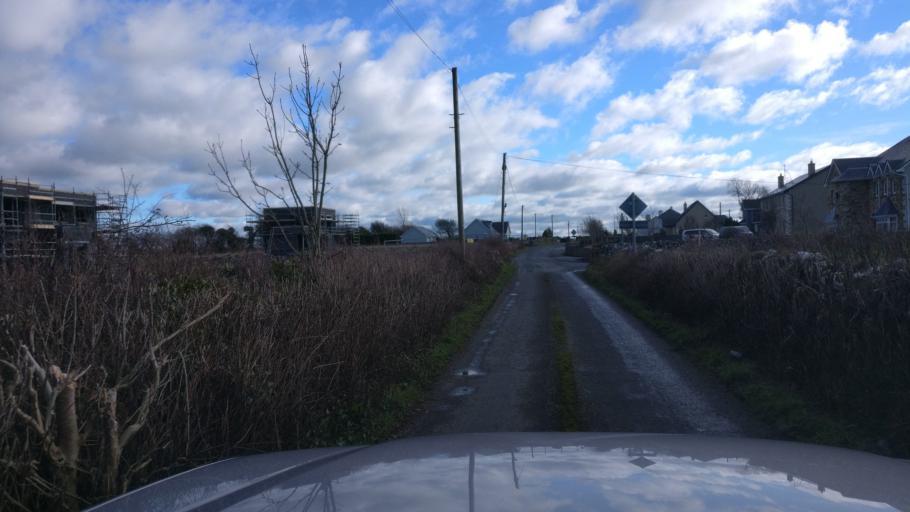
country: IE
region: Connaught
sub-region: County Galway
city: Oranmore
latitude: 53.2796
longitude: -8.8926
